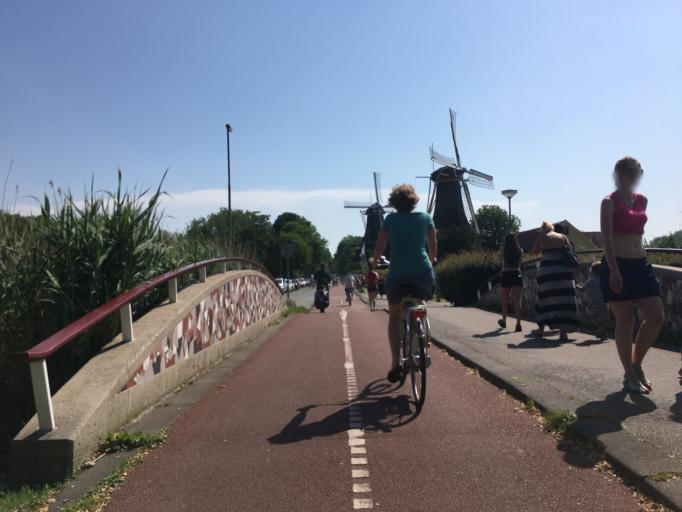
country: NL
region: South Holland
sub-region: Gemeente Rotterdam
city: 's-Gravenland
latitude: 51.9331
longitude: 4.5224
